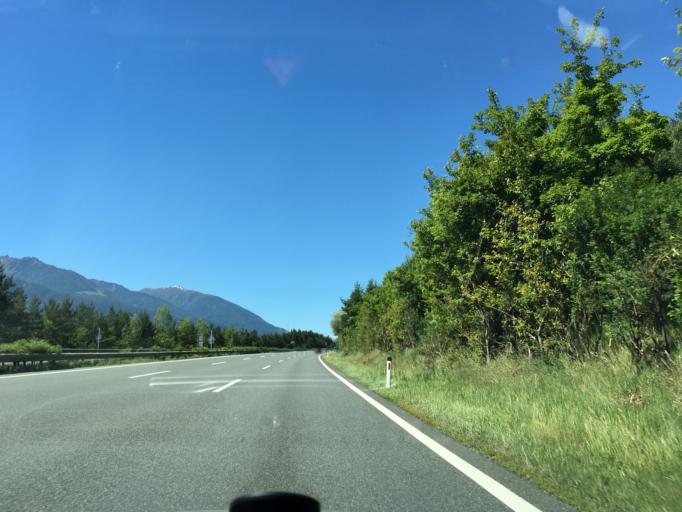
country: AT
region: Tyrol
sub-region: Politischer Bezirk Imst
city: Haiming
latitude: 47.2562
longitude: 10.8683
